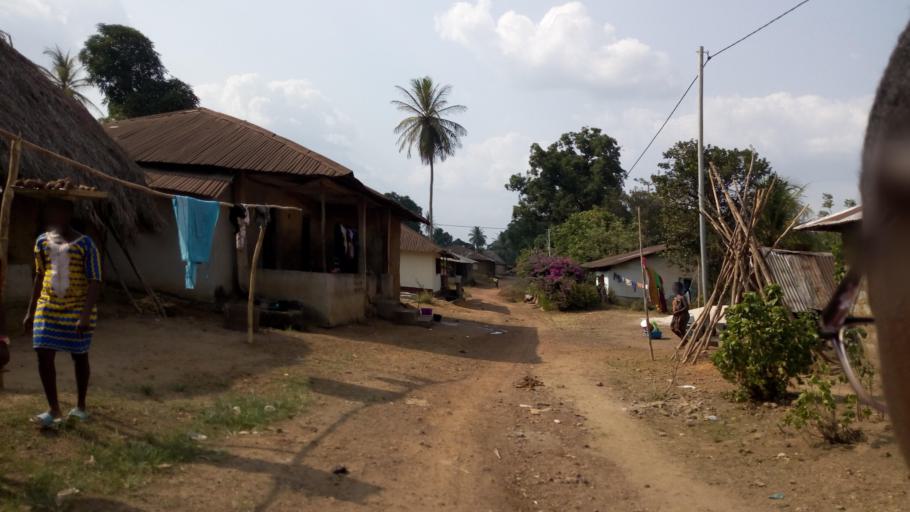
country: SL
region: Southern Province
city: Mogbwemo
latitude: 7.7644
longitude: -12.3071
